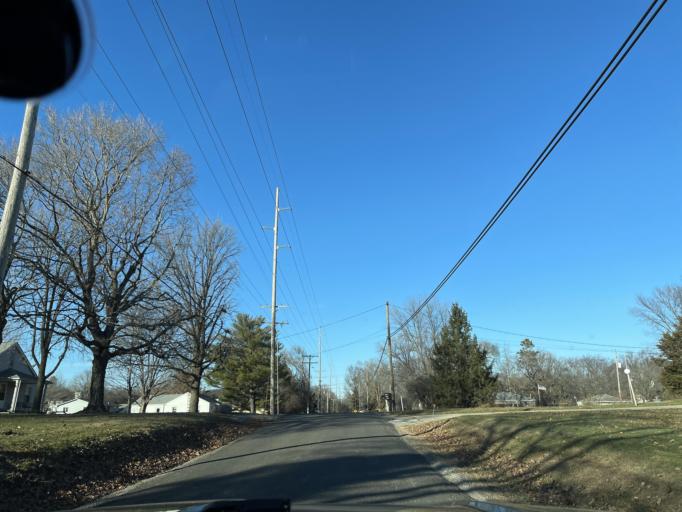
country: US
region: Illinois
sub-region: Sangamon County
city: Leland Grove
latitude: 39.8053
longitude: -89.7156
